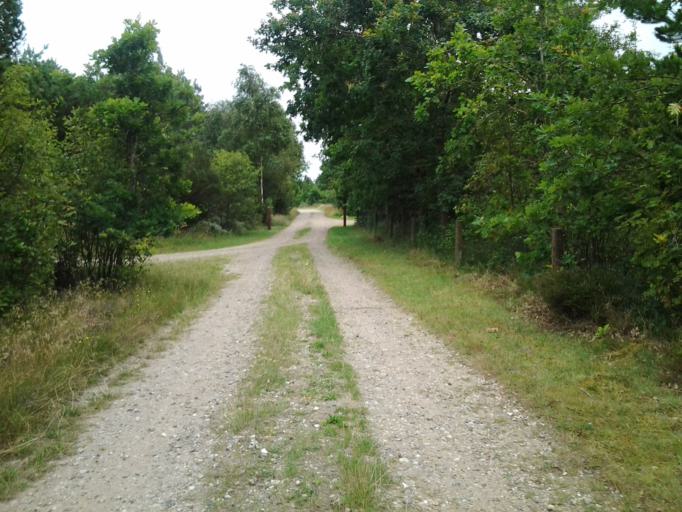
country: DE
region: Schleswig-Holstein
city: List
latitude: 55.1171
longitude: 8.5438
